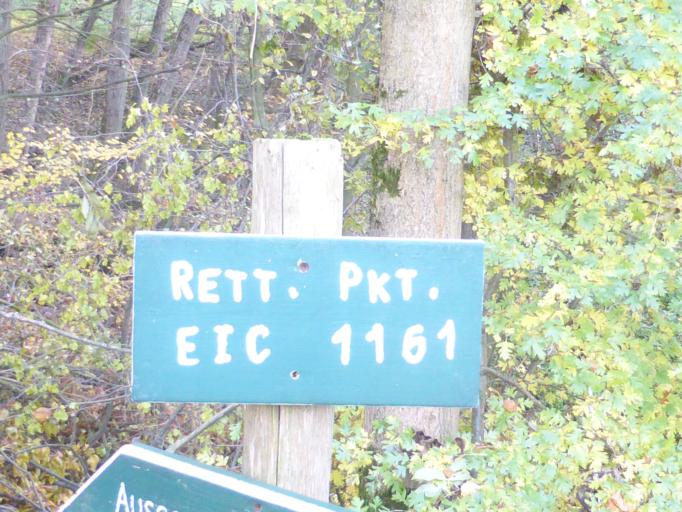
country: DE
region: Thuringia
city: Gerbershausen
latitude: 51.3322
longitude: 9.9678
